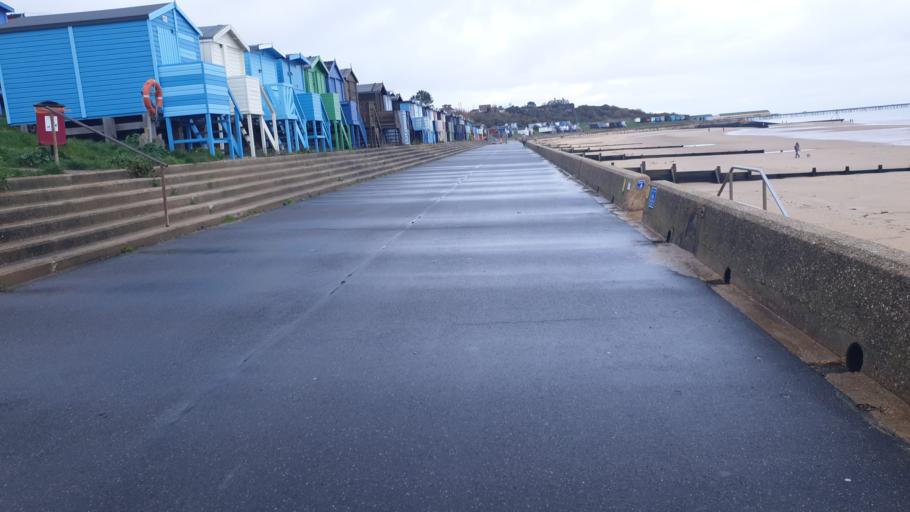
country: GB
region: England
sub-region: Essex
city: Walton-on-the-Naze
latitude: 51.8389
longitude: 1.2607
